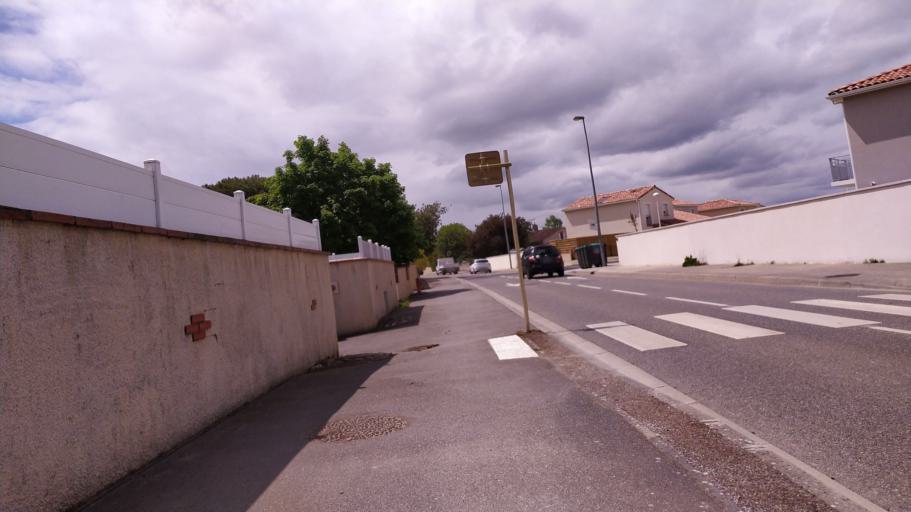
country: FR
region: Midi-Pyrenees
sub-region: Departement de la Haute-Garonne
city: Plaisance-du-Touch
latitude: 43.5816
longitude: 1.2956
